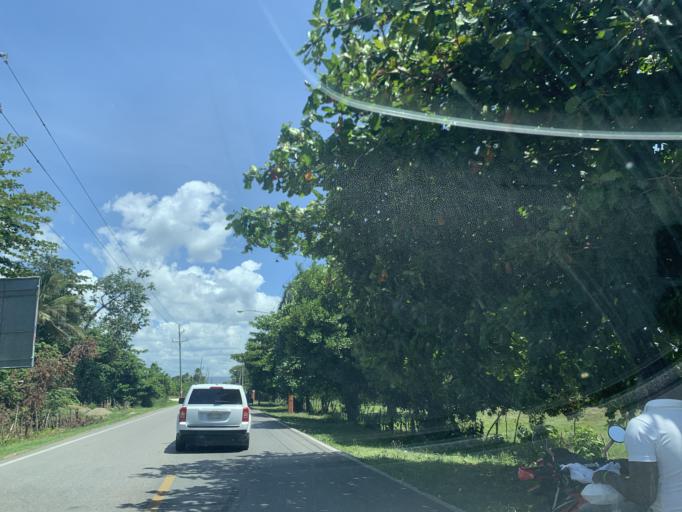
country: DO
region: Puerto Plata
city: Cabarete
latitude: 19.7265
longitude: -70.3877
